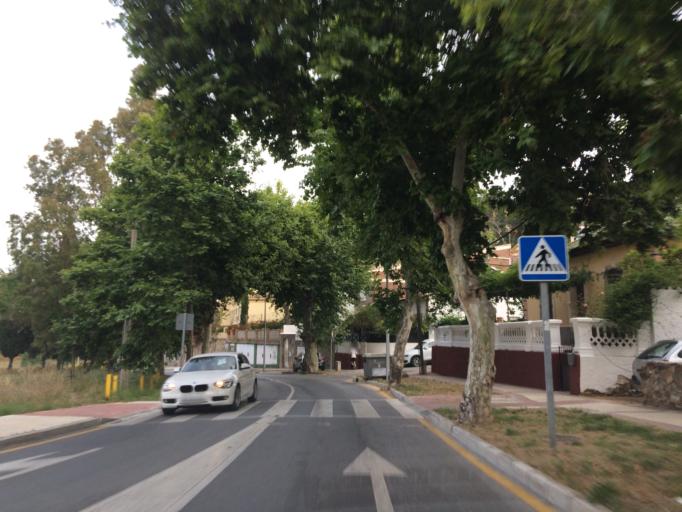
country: ES
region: Andalusia
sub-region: Provincia de Malaga
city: Malaga
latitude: 36.7269
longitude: -4.4057
